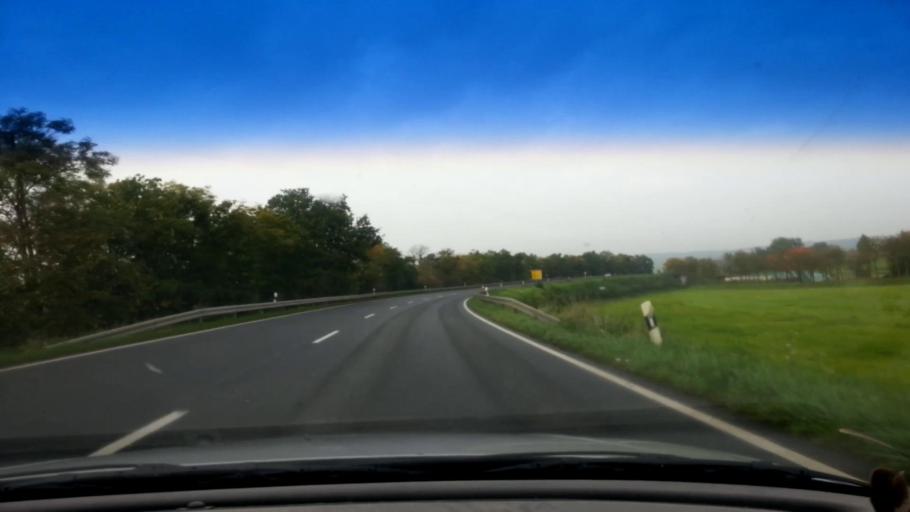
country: DE
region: Bavaria
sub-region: Upper Franconia
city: Rattelsdorf
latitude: 50.0410
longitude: 10.8818
